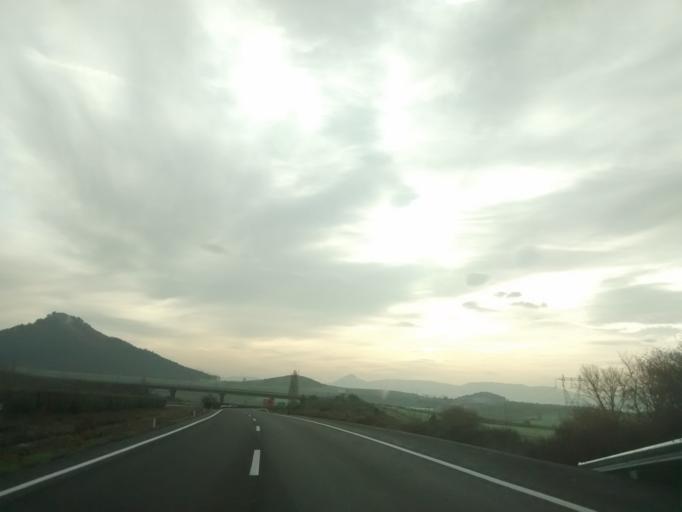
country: ES
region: Navarre
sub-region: Provincia de Navarra
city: Oltza
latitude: 42.8749
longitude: -1.7563
